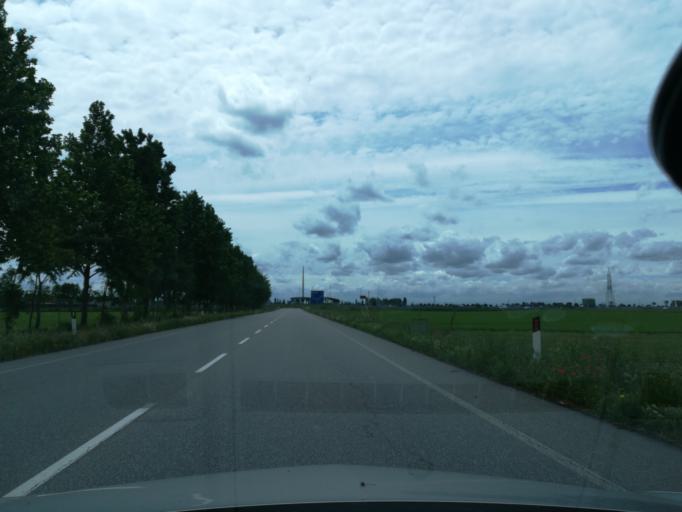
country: IT
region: Lombardy
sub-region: Provincia di Bergamo
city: Calcio
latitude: 45.5029
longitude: 9.8303
